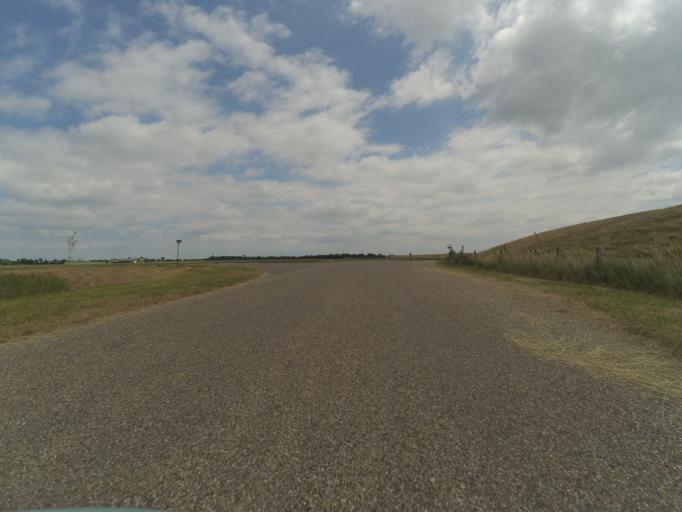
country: NL
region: Zeeland
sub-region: Gemeente Terneuzen
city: Terneuzen
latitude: 51.3978
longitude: 3.8811
